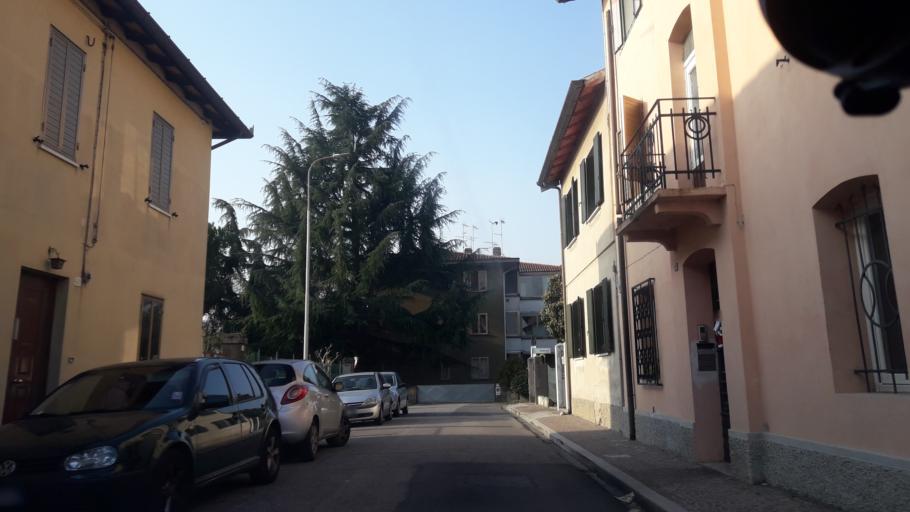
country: IT
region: Friuli Venezia Giulia
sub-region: Provincia di Udine
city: Udine
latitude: 46.0475
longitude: 13.2280
